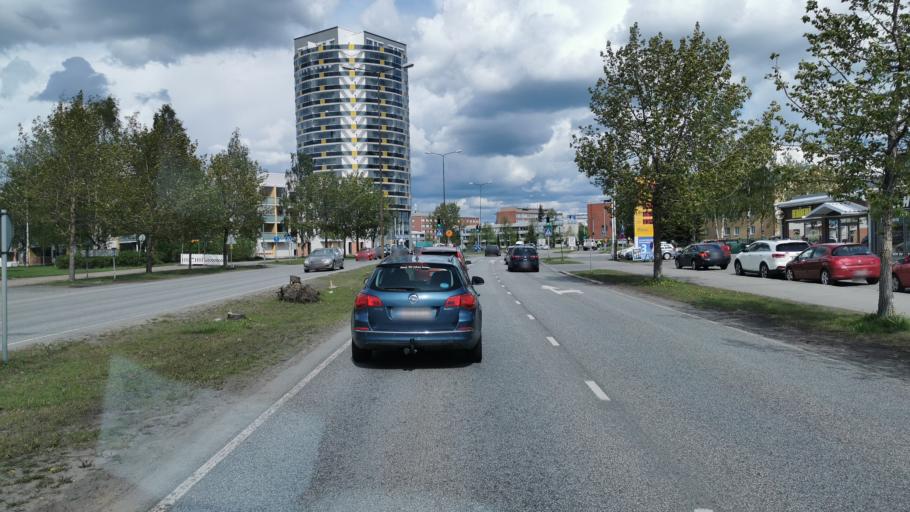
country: FI
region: Northern Ostrobothnia
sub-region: Oulu
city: Oulu
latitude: 65.0022
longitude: 25.4637
